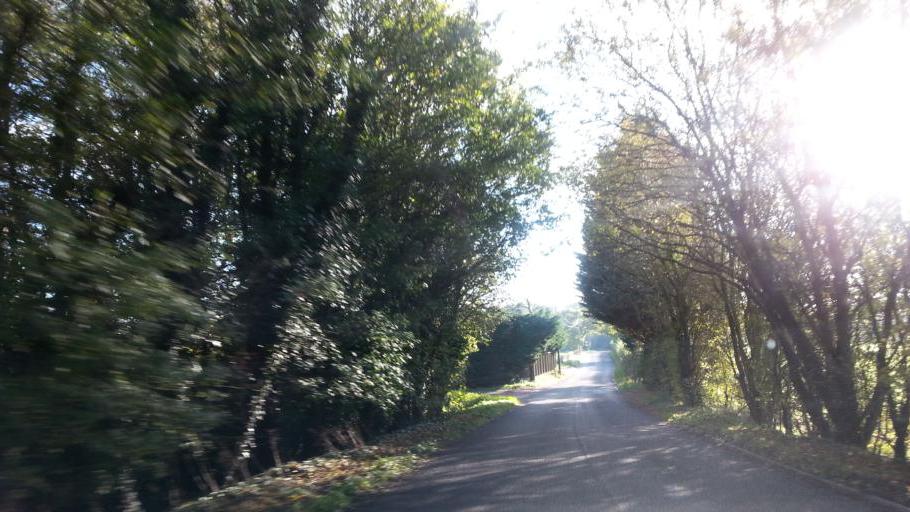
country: GB
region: England
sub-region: Suffolk
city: Thurston
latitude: 52.2358
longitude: 0.8076
